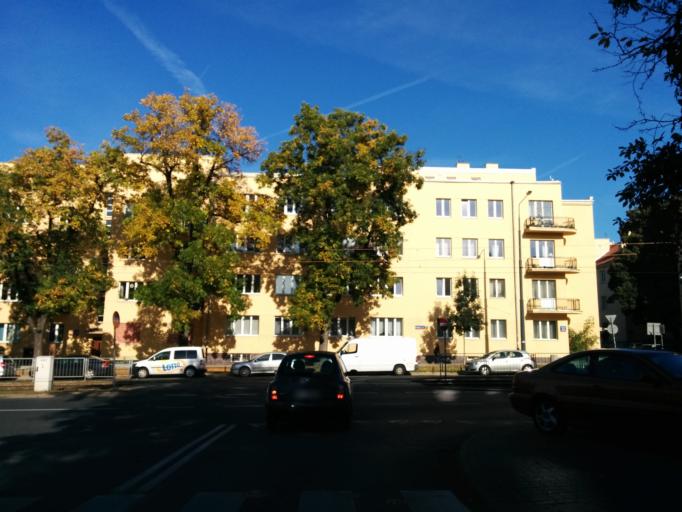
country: PL
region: Masovian Voivodeship
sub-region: Warszawa
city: Zoliborz
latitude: 52.2705
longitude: 20.9844
